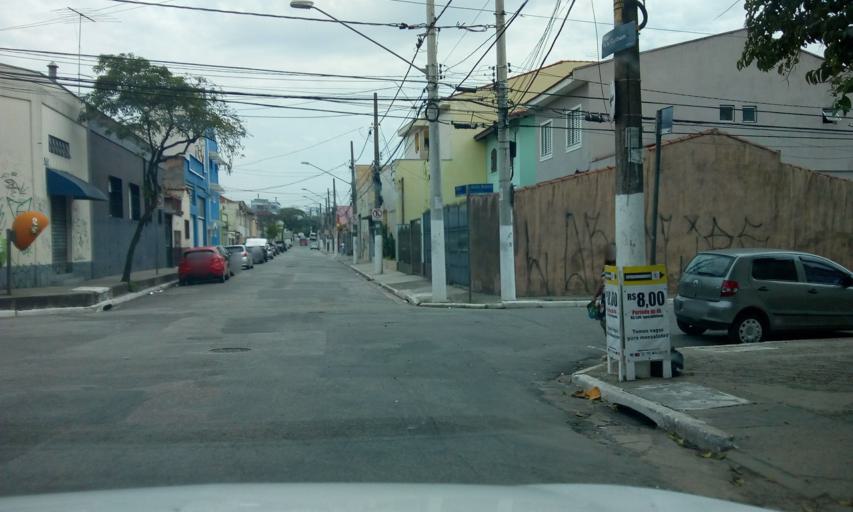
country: BR
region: Sao Paulo
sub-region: Sao Paulo
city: Sao Paulo
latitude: -23.5179
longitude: -46.7005
